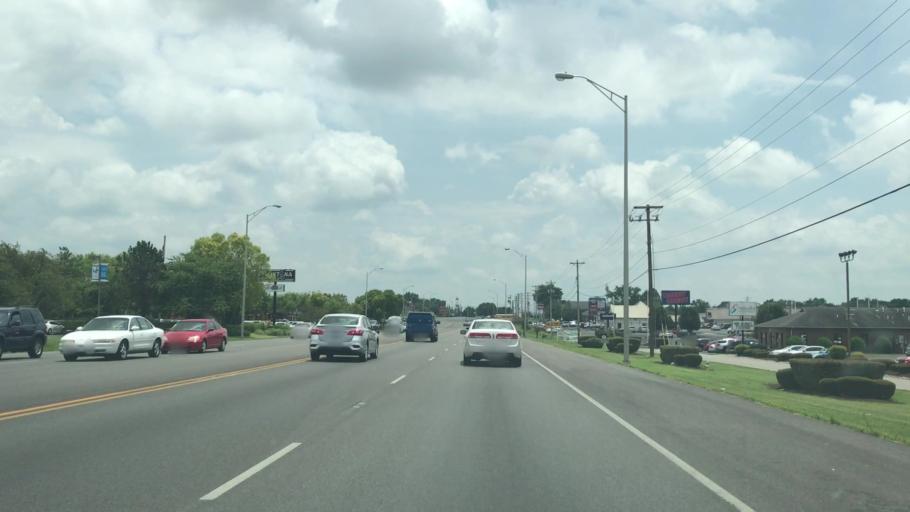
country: US
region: Kentucky
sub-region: Warren County
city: Bowling Green
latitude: 36.9692
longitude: -86.4338
